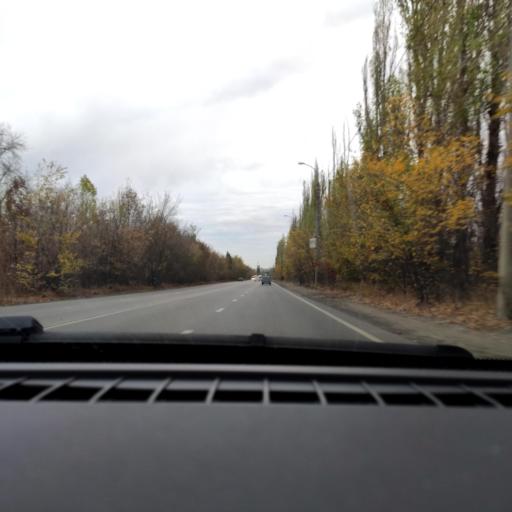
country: RU
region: Voronezj
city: Maslovka
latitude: 51.6078
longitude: 39.2557
